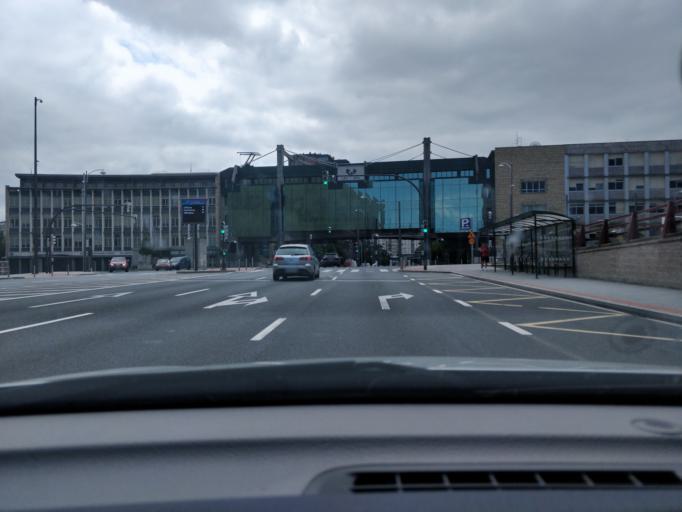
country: ES
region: Basque Country
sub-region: Bizkaia
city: Bilbao
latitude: 43.2629
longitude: -2.9508
